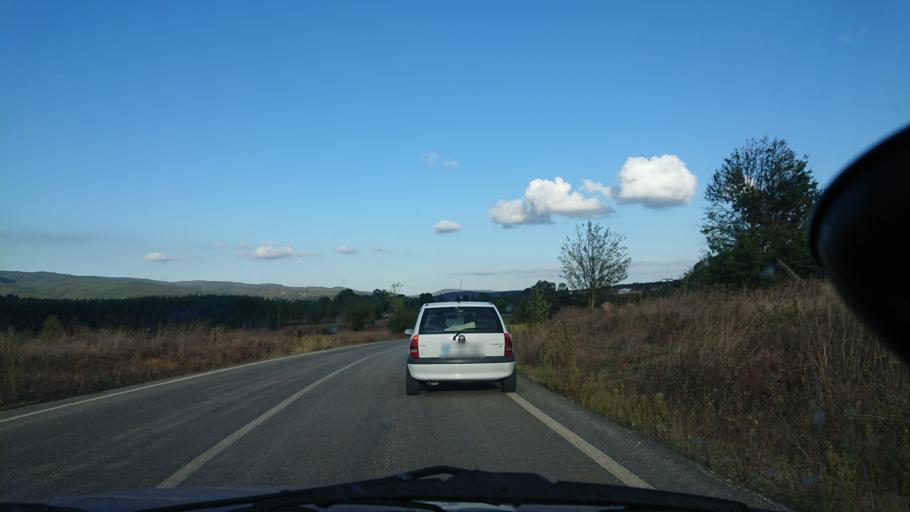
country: TR
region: Bilecik
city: Pazaryeri
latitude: 40.0120
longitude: 29.8203
